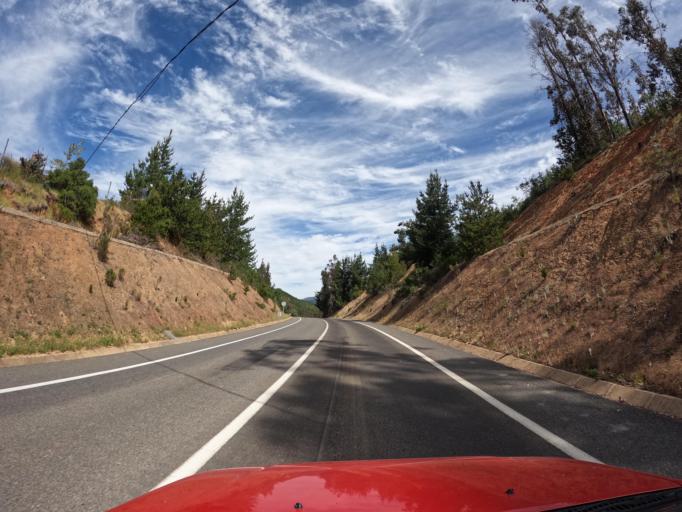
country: CL
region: Maule
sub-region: Provincia de Talca
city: Talca
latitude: -35.1516
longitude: -71.9622
